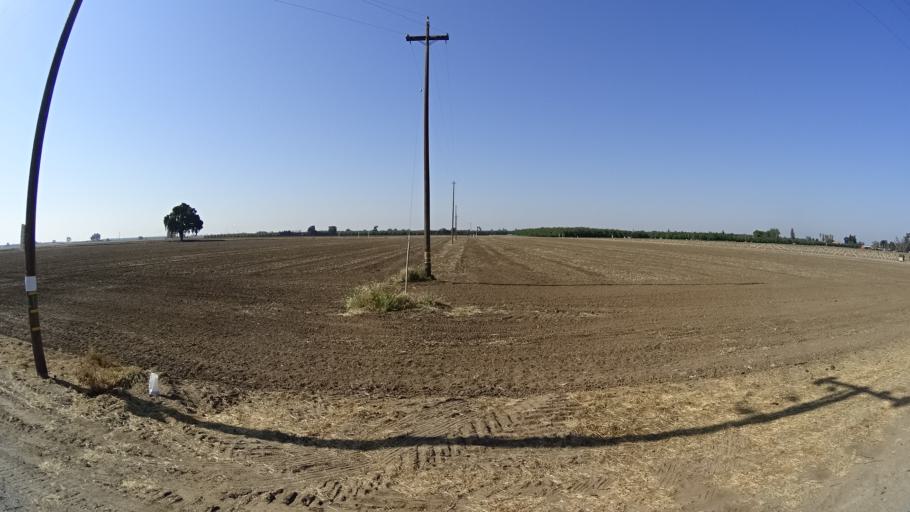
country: US
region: California
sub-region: Kings County
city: Lucerne
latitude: 36.3864
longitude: -119.6461
